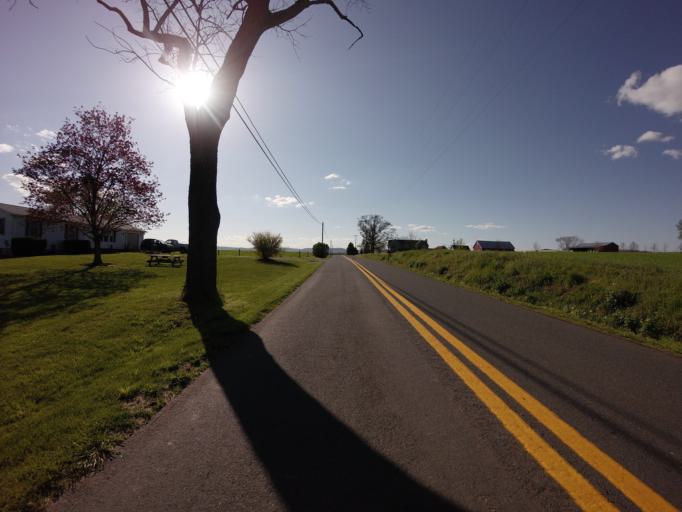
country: US
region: Maryland
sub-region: Frederick County
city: Woodsboro
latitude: 39.6203
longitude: -77.2786
